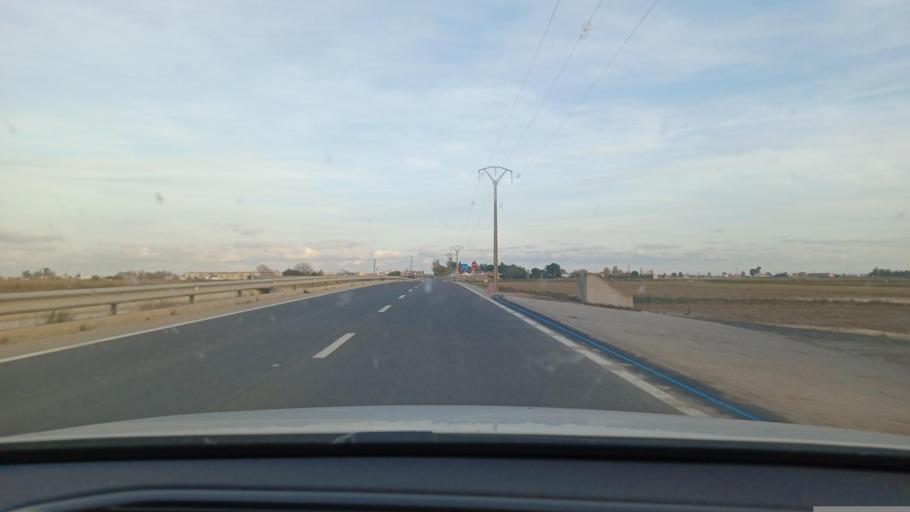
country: ES
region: Catalonia
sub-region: Provincia de Tarragona
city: Deltebre
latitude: 40.7068
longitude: 0.7003
